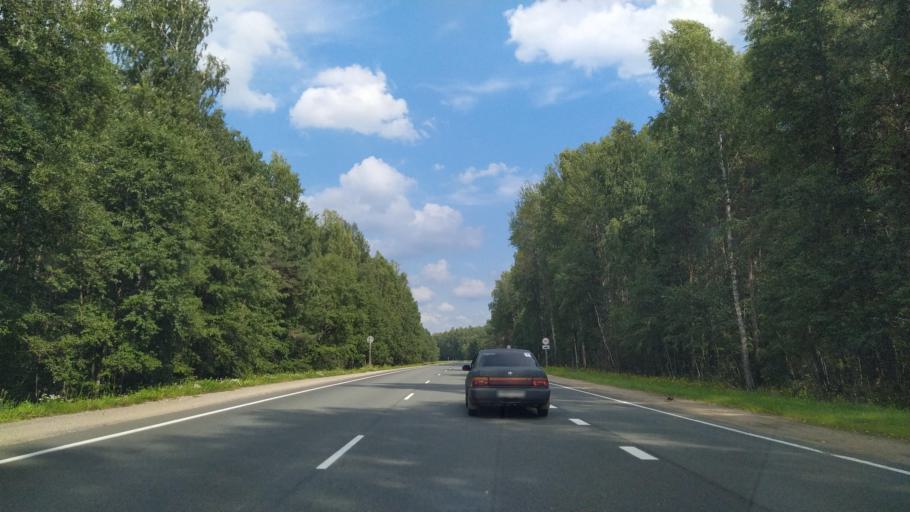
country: RU
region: Pskov
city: Porkhov
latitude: 57.8637
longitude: 29.5855
